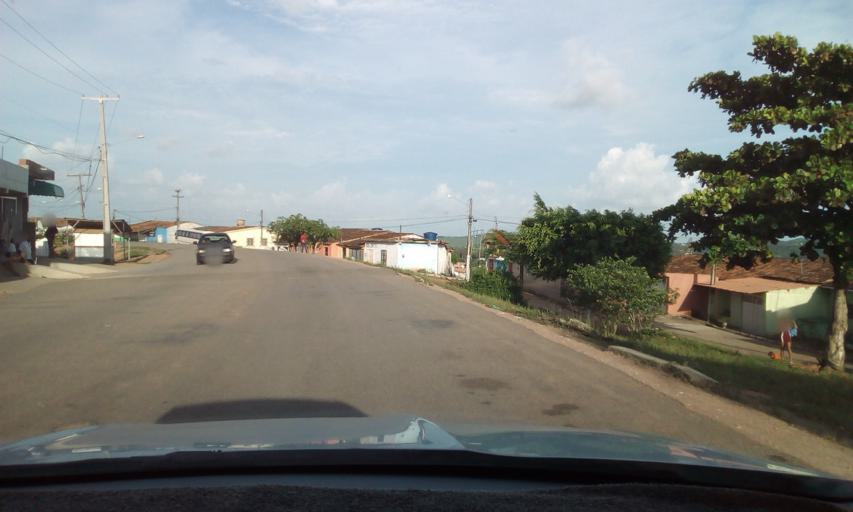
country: BR
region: Pernambuco
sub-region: Gloria Do Goita
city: Gloria do Goita
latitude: -7.9951
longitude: -35.2095
